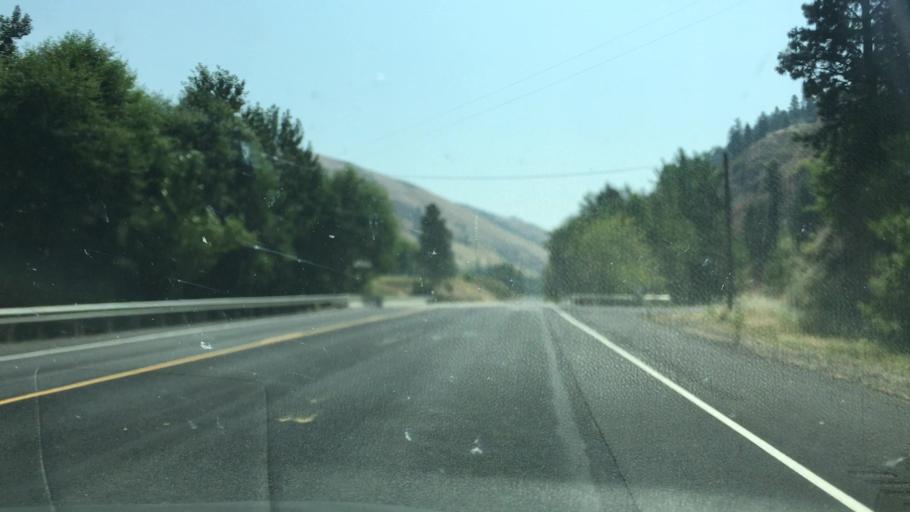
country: US
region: Idaho
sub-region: Nez Perce County
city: Lapwai
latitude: 46.3683
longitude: -116.6466
